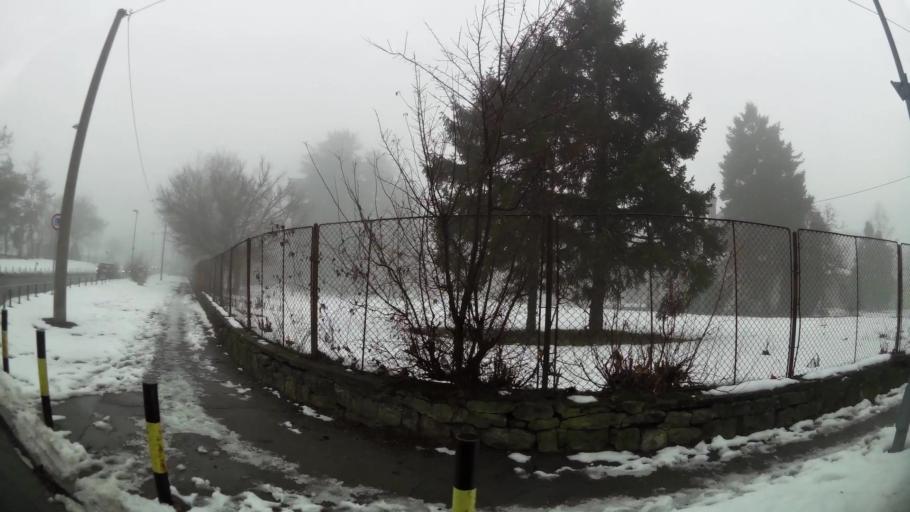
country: RS
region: Central Serbia
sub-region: Belgrade
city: Savski Venac
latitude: 44.7681
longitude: 20.4613
